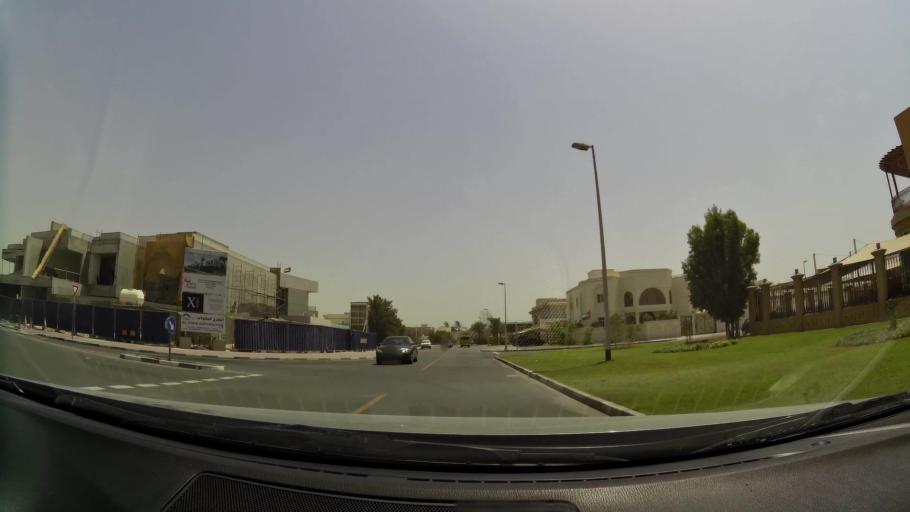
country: AE
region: Dubai
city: Dubai
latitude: 25.1300
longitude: 55.2038
